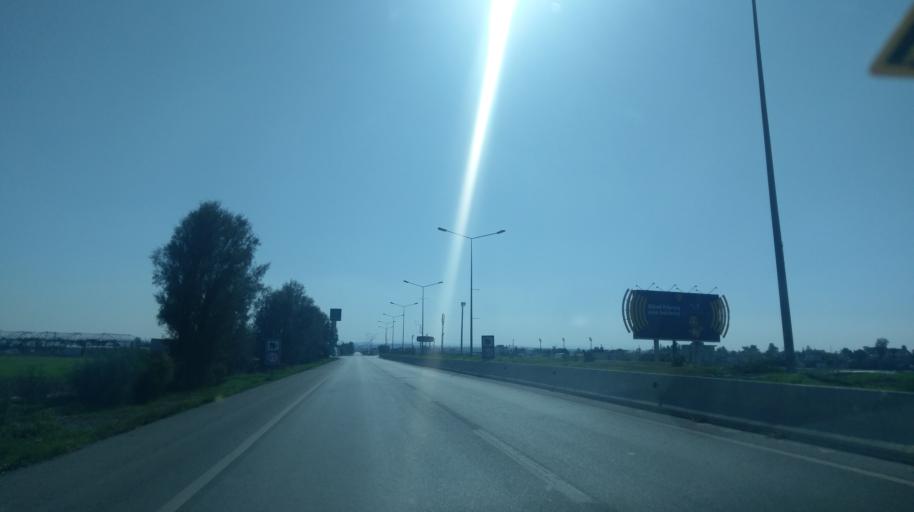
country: CY
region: Lefkosia
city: Geri
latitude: 35.2116
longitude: 33.4983
